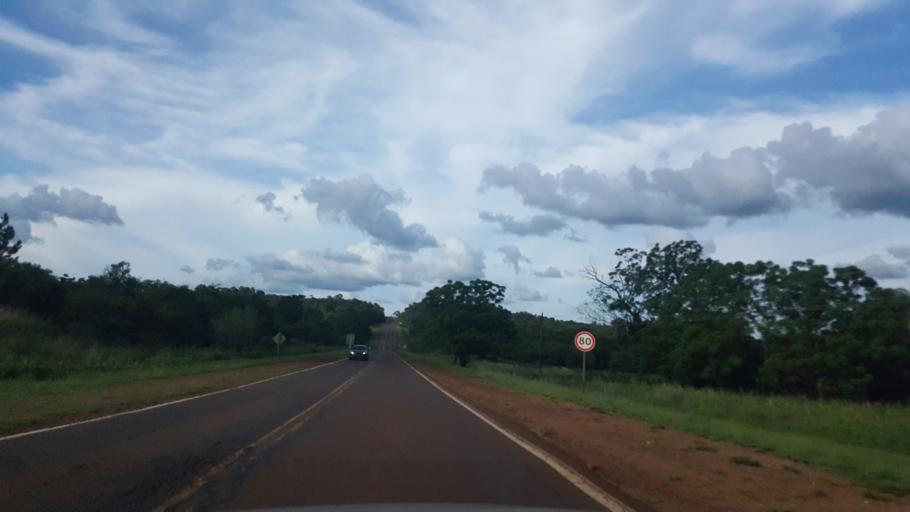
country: AR
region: Misiones
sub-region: Departamento de San Ignacio
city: San Ignacio
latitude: -27.2527
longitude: -55.5235
